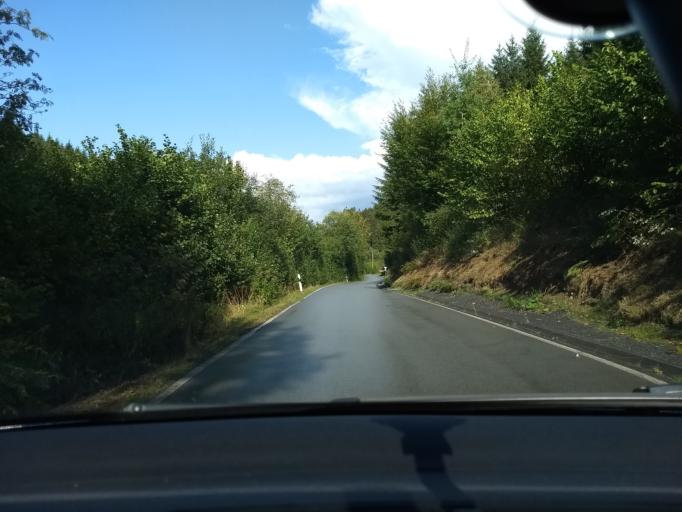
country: DE
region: North Rhine-Westphalia
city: Eslohe
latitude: 51.2395
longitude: 8.0713
